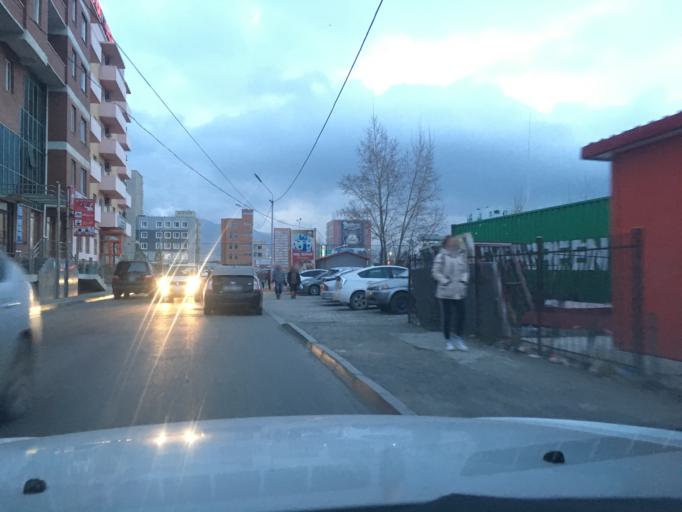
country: MN
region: Ulaanbaatar
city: Ulaanbaatar
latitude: 47.9144
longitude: 106.8602
